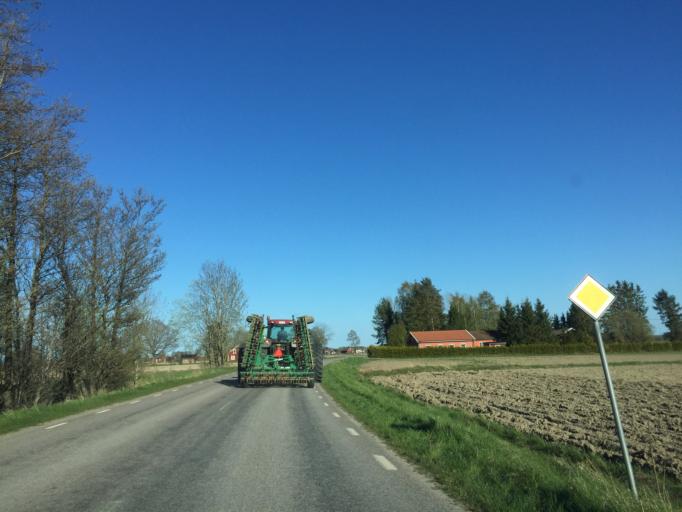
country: SE
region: OErebro
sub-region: Orebro Kommun
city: Odensbacken
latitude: 59.2046
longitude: 15.5267
